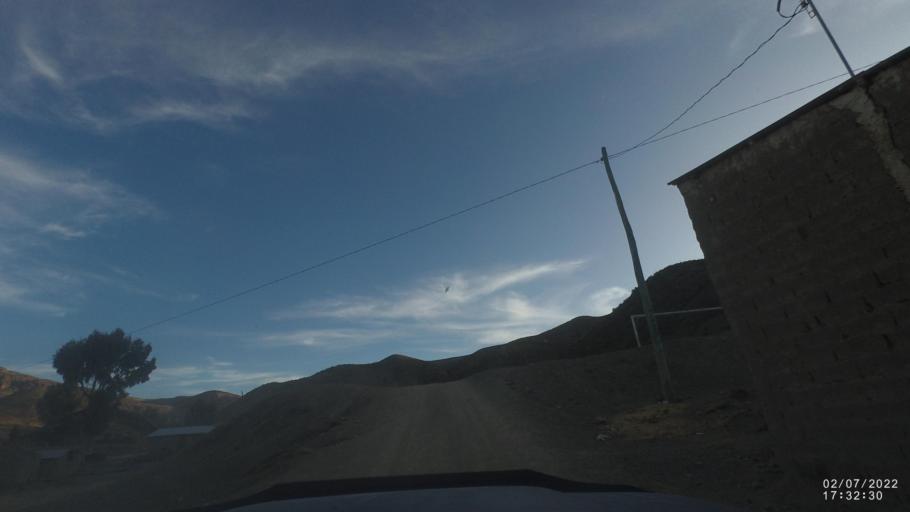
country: BO
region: Cochabamba
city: Irpa Irpa
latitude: -17.8841
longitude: -66.6176
